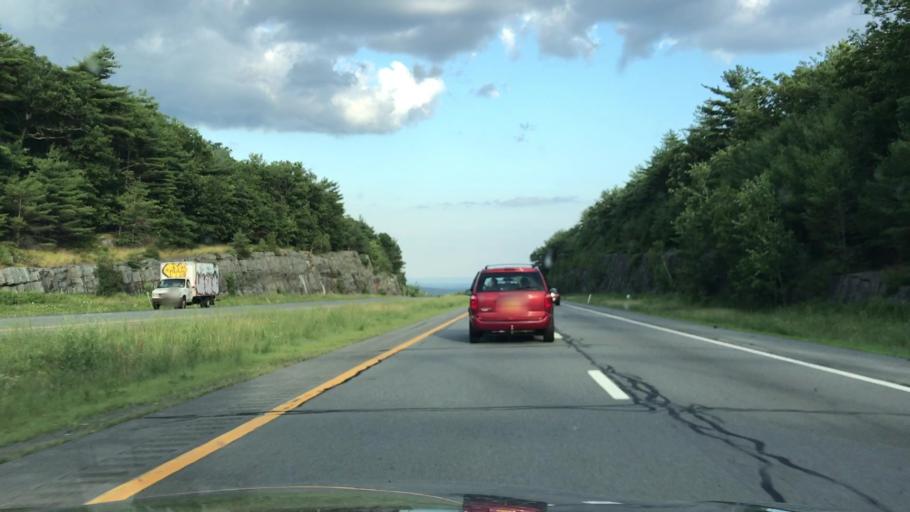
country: US
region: New York
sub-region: Sullivan County
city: Wurtsboro
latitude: 41.5965
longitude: -74.5423
